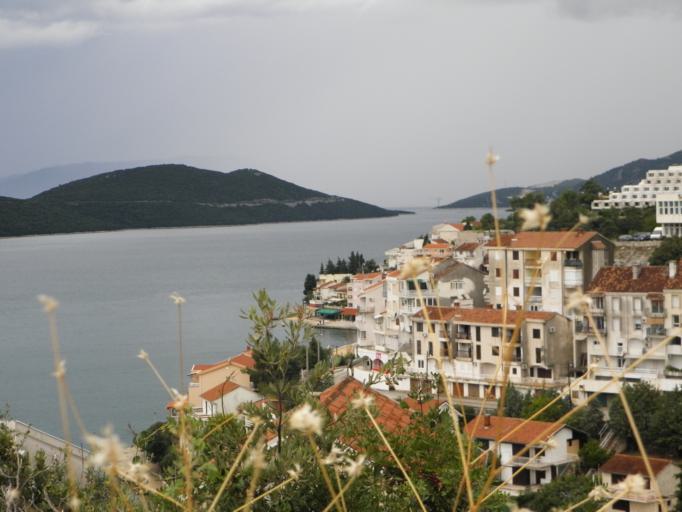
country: BA
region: Federation of Bosnia and Herzegovina
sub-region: Hercegovacko-Bosanski Kanton
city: Neum
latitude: 42.9425
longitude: 17.5654
